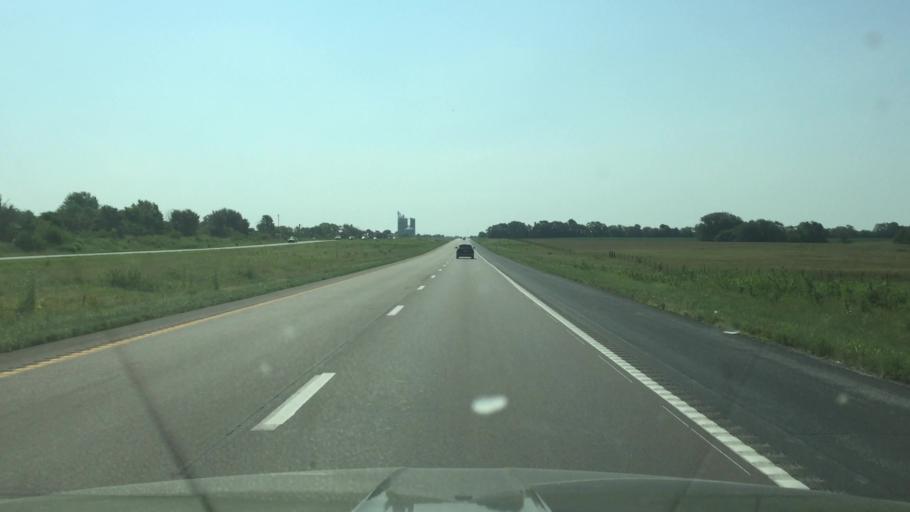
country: US
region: Missouri
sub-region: Pettis County
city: La Monte
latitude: 38.7582
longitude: -93.3688
